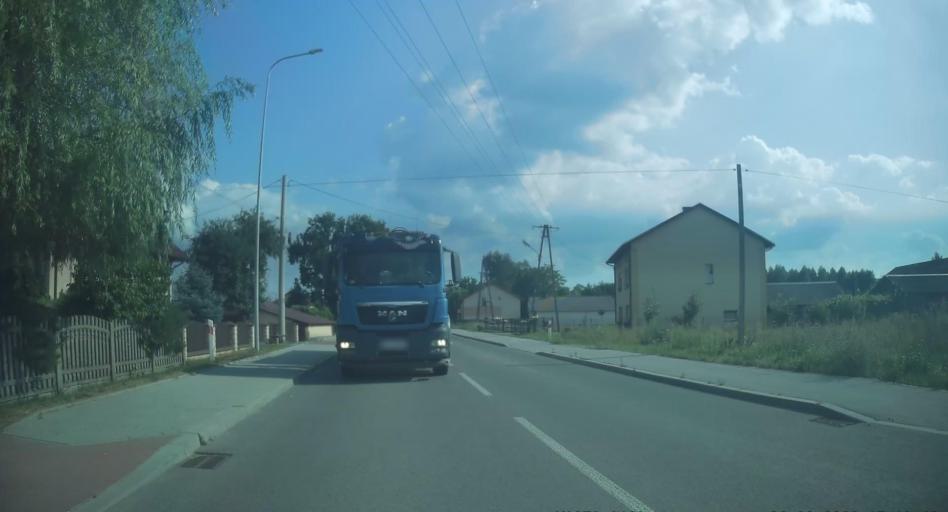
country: PL
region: Swietokrzyskie
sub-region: Powiat konecki
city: Radoszyce
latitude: 51.0520
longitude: 20.2809
